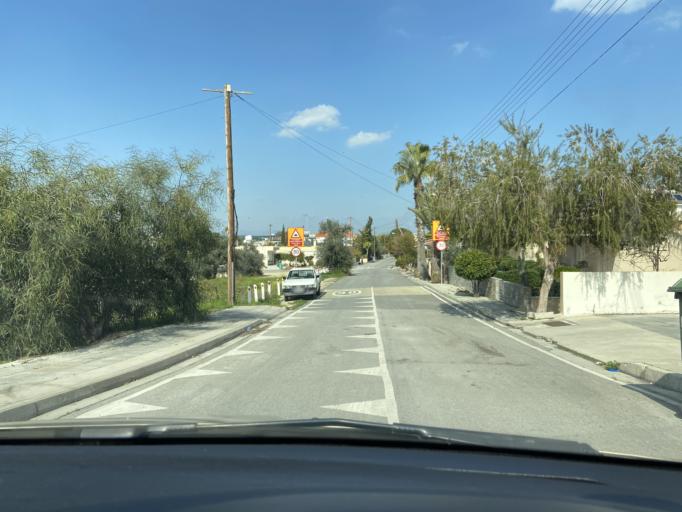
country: CY
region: Lefkosia
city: Alampra
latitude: 35.0100
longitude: 33.3880
